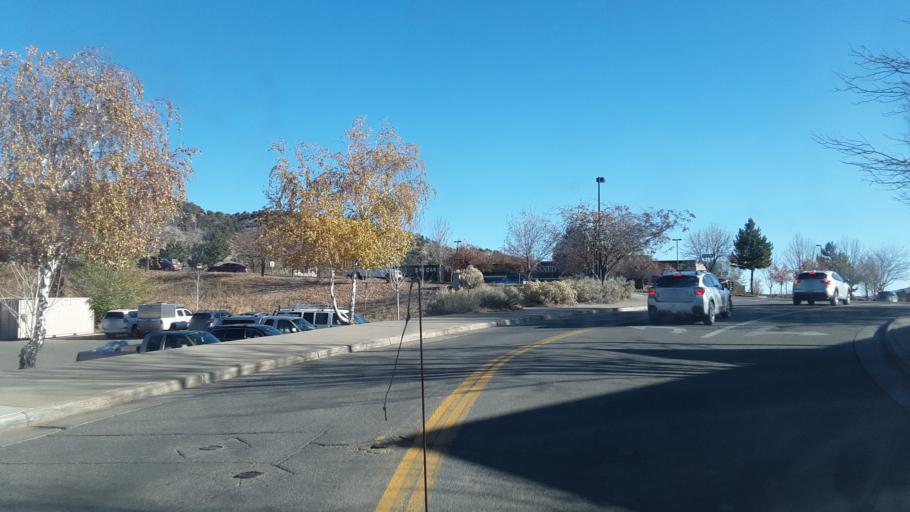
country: US
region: Colorado
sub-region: La Plata County
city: Durango
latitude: 37.2296
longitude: -107.8638
